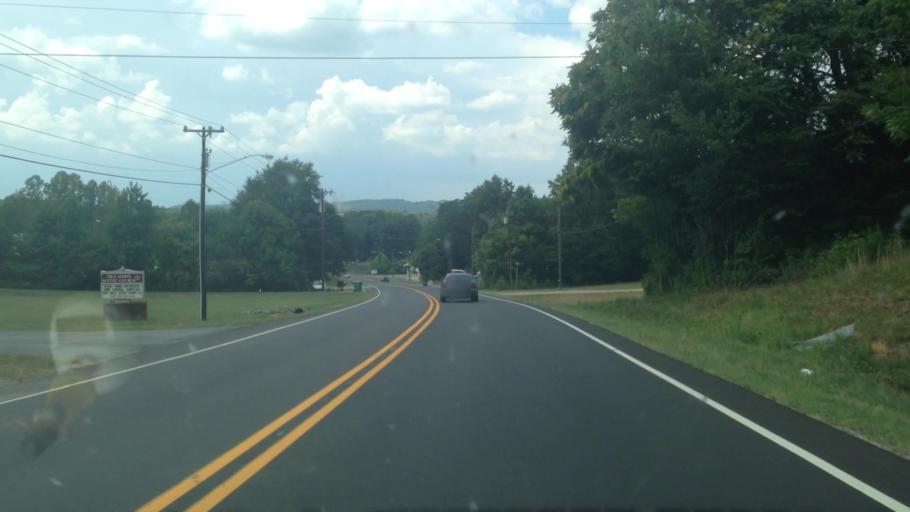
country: US
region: North Carolina
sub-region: Rockingham County
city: Madison
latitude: 36.3815
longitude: -79.9481
